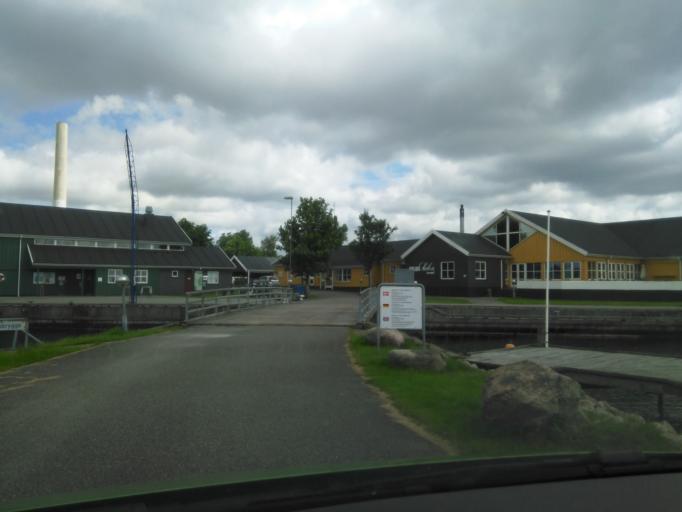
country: DK
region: Central Jutland
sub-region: Arhus Kommune
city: Logten
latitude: 56.2439
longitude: 10.3420
